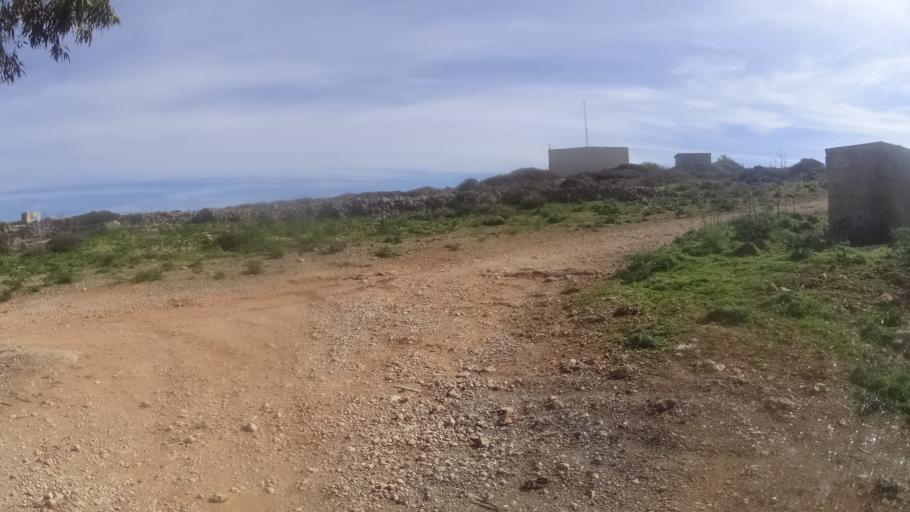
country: MT
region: Il-Qala
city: Qala
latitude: 36.0091
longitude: 14.3320
